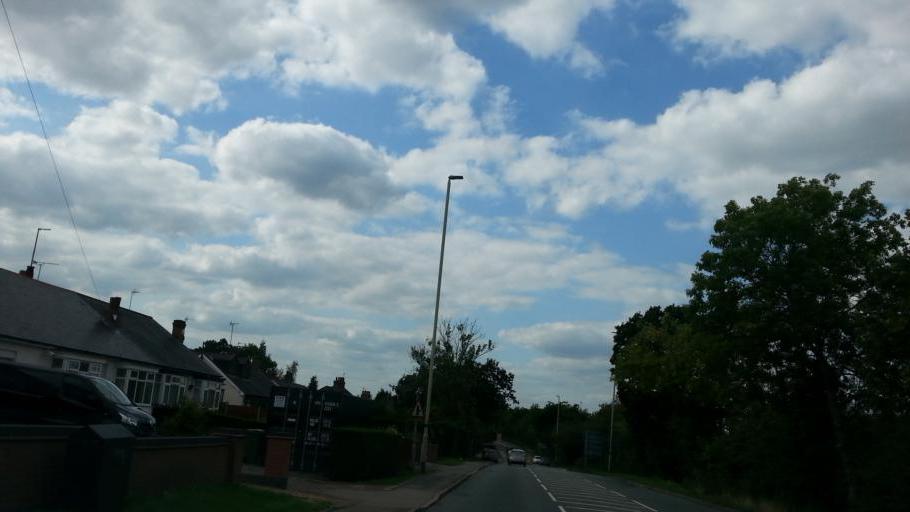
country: GB
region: England
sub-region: Leicestershire
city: Glenfield
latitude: 52.6273
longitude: -1.2018
